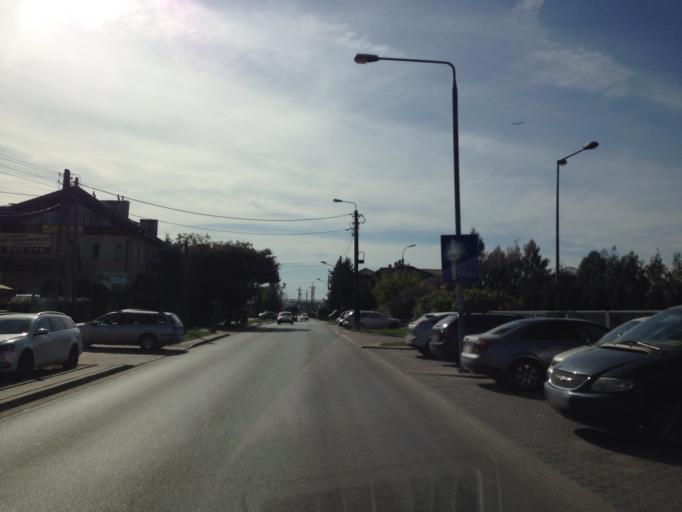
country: PL
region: Masovian Voivodeship
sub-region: Warszawa
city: Wlochy
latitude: 52.1882
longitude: 20.9436
